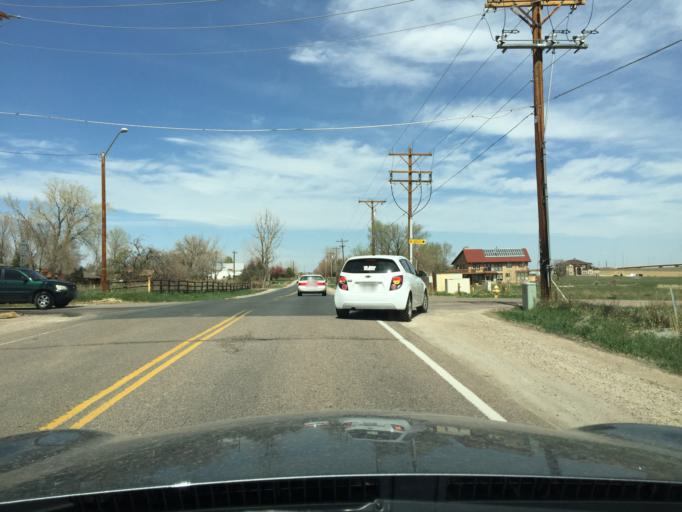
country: US
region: Colorado
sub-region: Adams County
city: Northglenn
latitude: 39.9718
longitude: -104.9971
